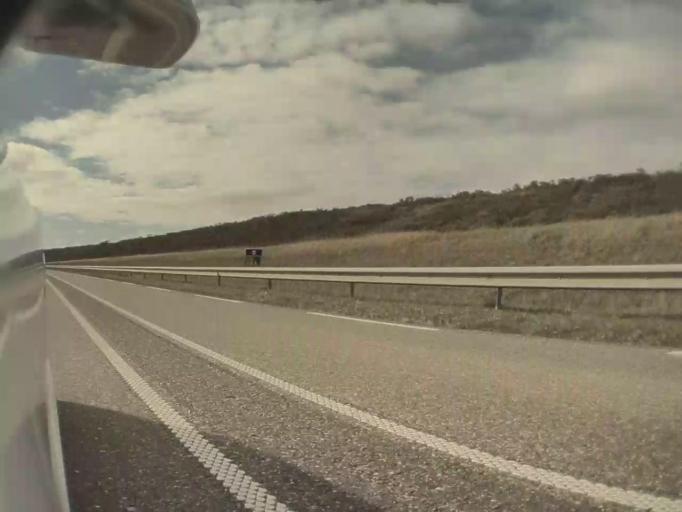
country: NL
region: Zeeland
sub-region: Gemeente Veere
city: Veere
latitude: 51.5888
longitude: 3.6451
